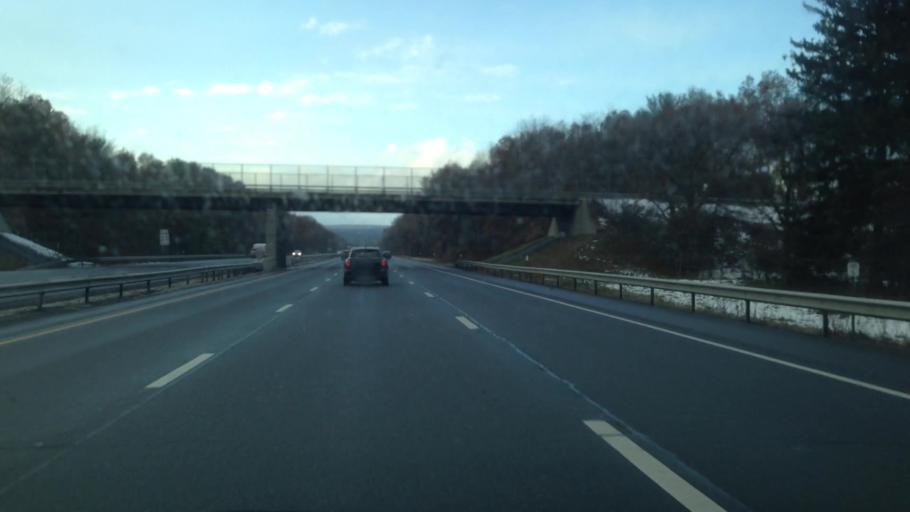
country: US
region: New York
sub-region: Schenectady County
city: Rotterdam
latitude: 42.7671
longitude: -73.9612
